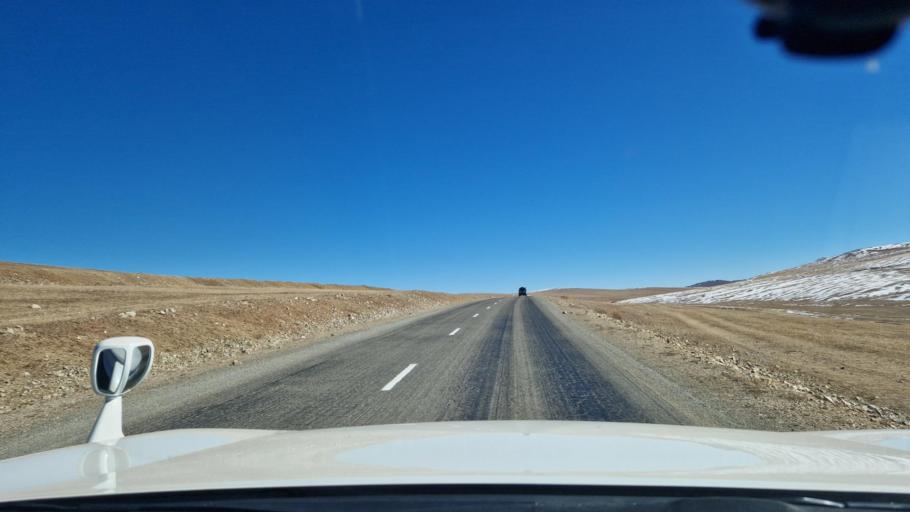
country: MN
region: Hentiy
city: Modot
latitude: 47.8055
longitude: 108.7158
